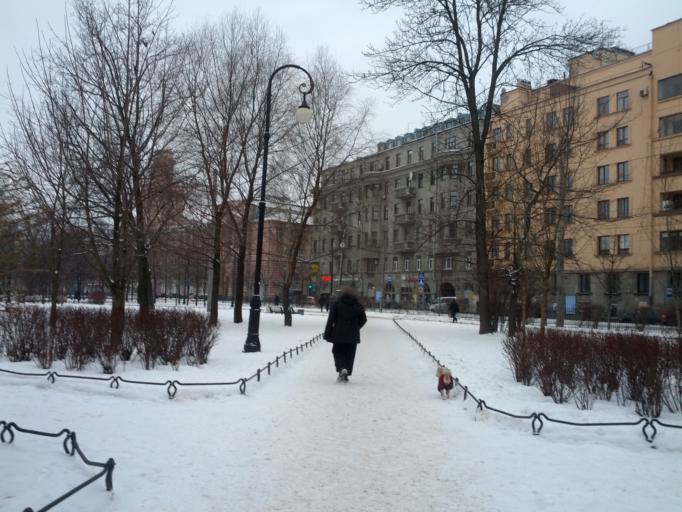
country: RU
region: St.-Petersburg
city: Petrogradka
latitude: 59.9566
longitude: 30.3136
